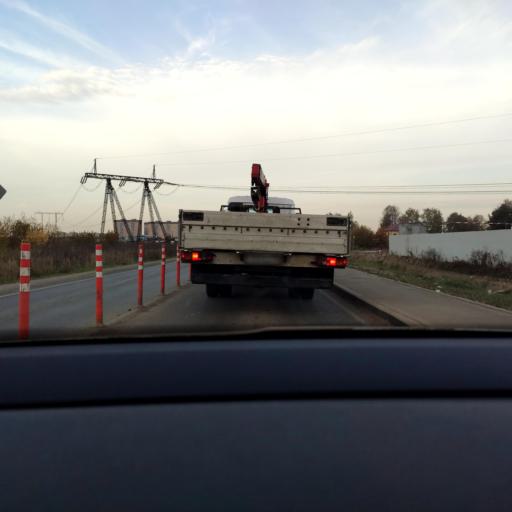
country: RU
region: Moskovskaya
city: Pirogovskiy
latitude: 55.9695
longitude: 37.7559
